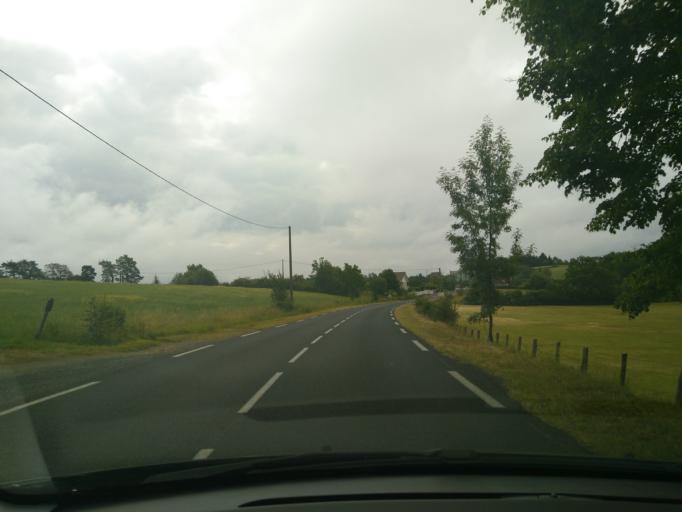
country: FR
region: Limousin
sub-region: Departement de la Correze
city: Cosnac
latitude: 45.1039
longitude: 1.5533
